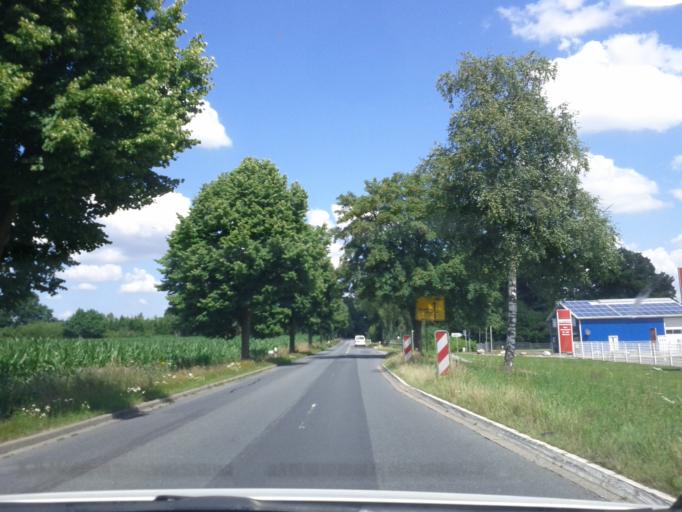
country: DE
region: Lower Saxony
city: Sauensiek
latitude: 53.3763
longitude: 9.5951
